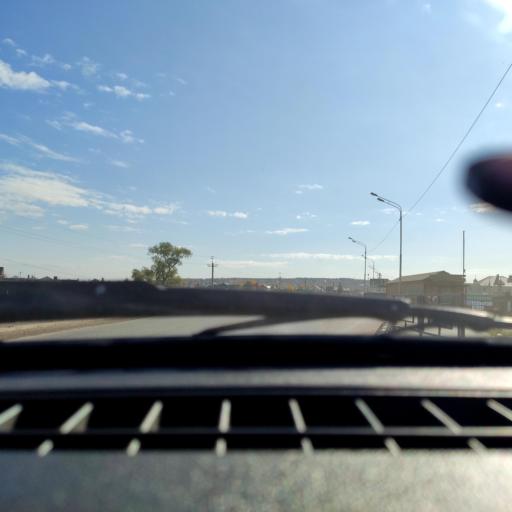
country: RU
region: Bashkortostan
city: Ufa
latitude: 54.6167
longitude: 55.9327
